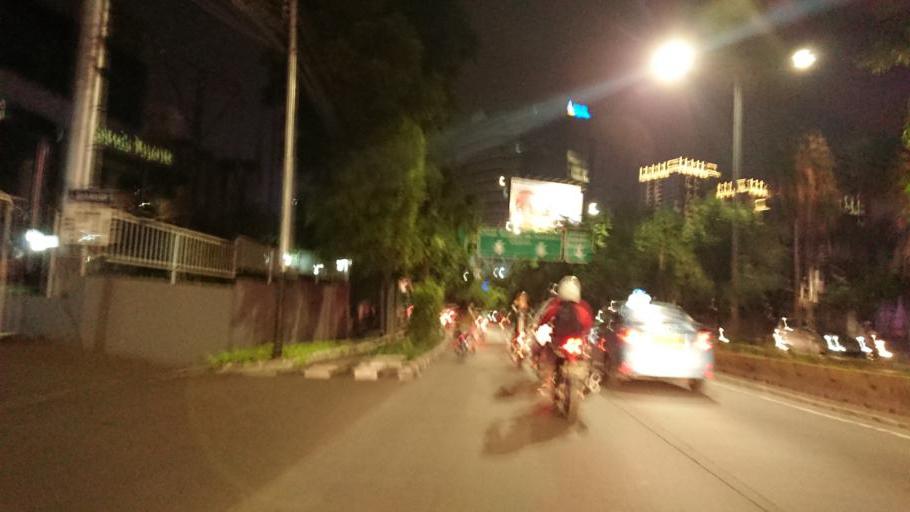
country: ID
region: Banten
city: South Tangerang
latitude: -6.2601
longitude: 106.7818
